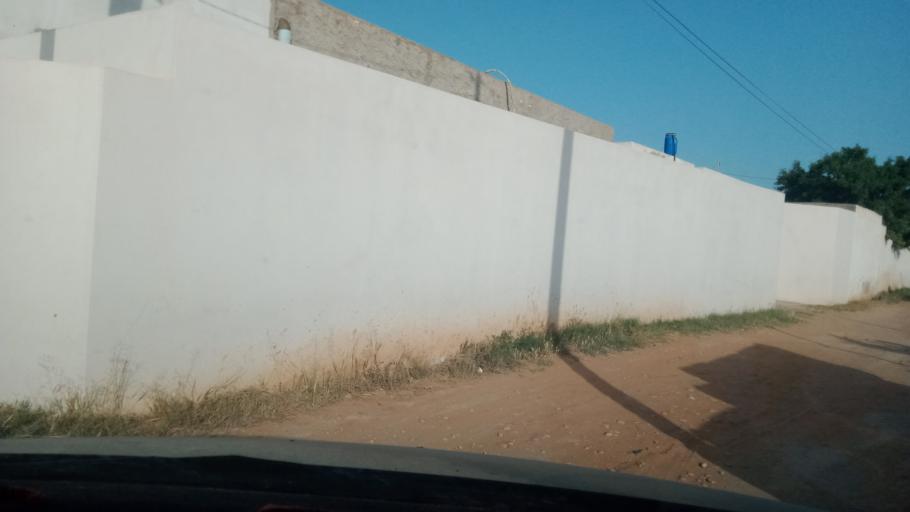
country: TN
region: Safaqis
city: Sfax
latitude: 34.8193
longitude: 10.7380
